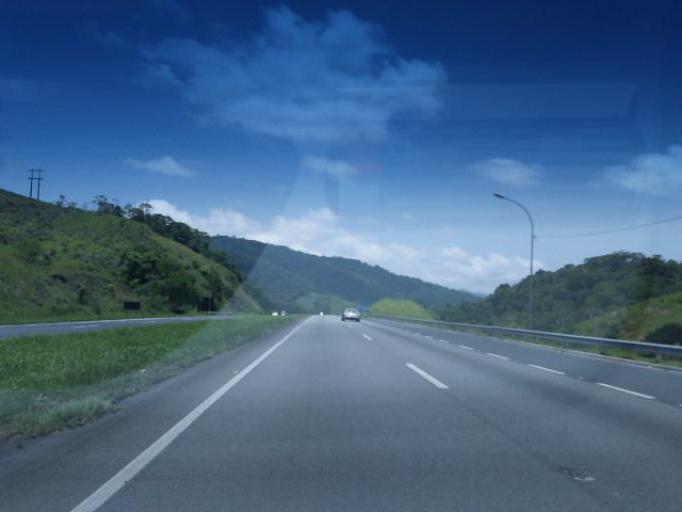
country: BR
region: Sao Paulo
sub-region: Miracatu
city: Miracatu
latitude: -24.2966
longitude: -47.4814
